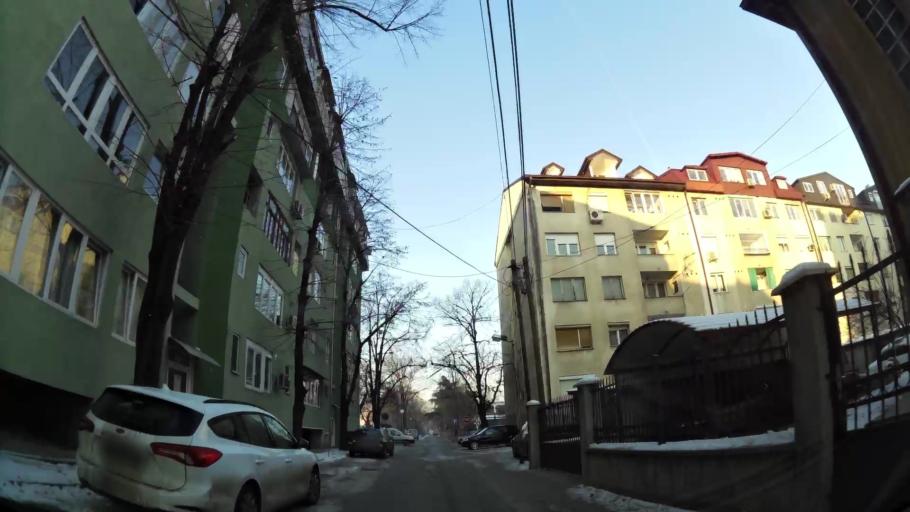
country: MK
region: Karpos
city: Skopje
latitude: 42.0037
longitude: 21.4111
